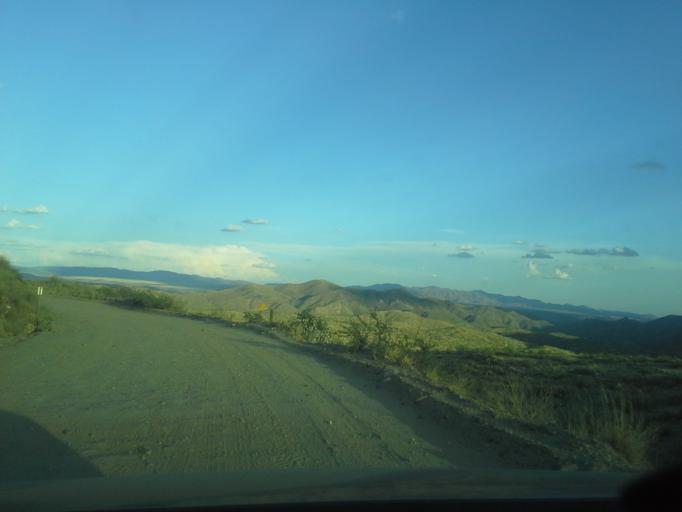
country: US
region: Arizona
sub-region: Yavapai County
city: Spring Valley
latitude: 34.2754
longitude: -112.2457
